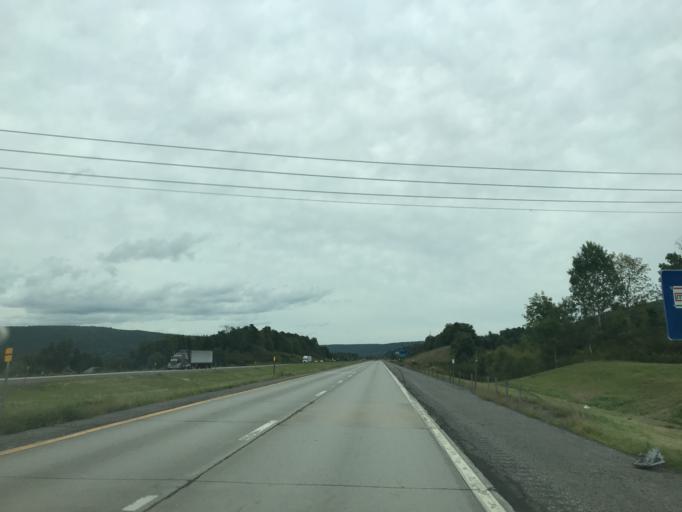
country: US
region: New York
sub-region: Otsego County
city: Oneonta
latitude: 42.4783
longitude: -74.9826
